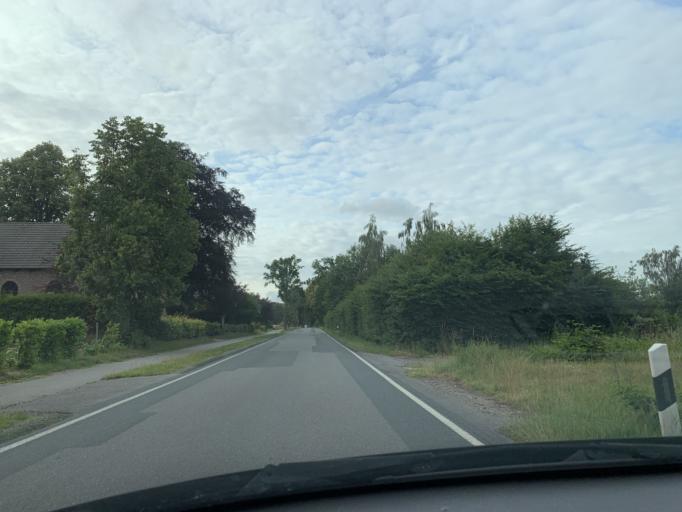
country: DE
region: Lower Saxony
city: Westerstede
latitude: 53.2825
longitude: 7.9253
